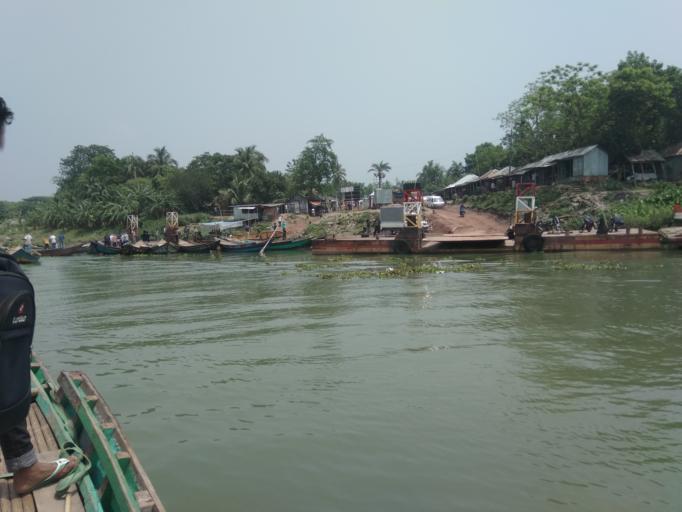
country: BD
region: Khulna
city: Kalia
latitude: 23.1951
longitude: 89.6931
